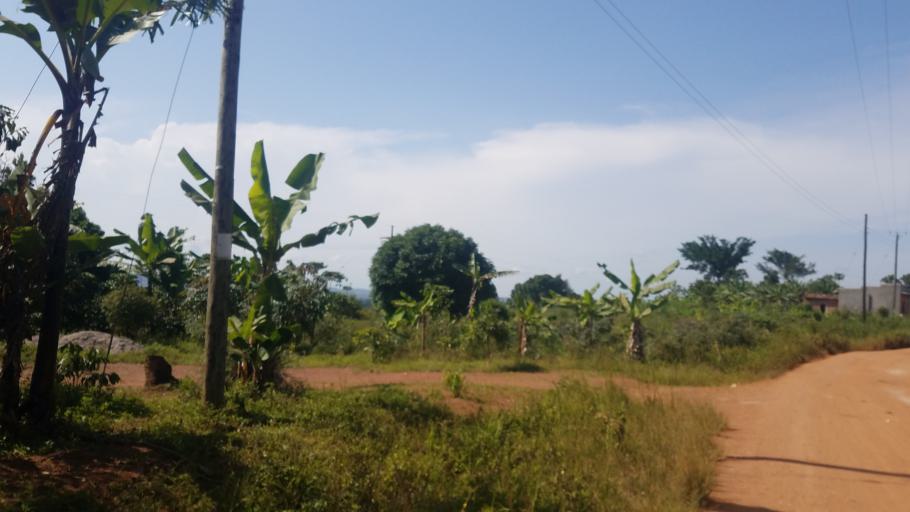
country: UG
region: Central Region
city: Masaka
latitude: -0.3050
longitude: 31.6834
